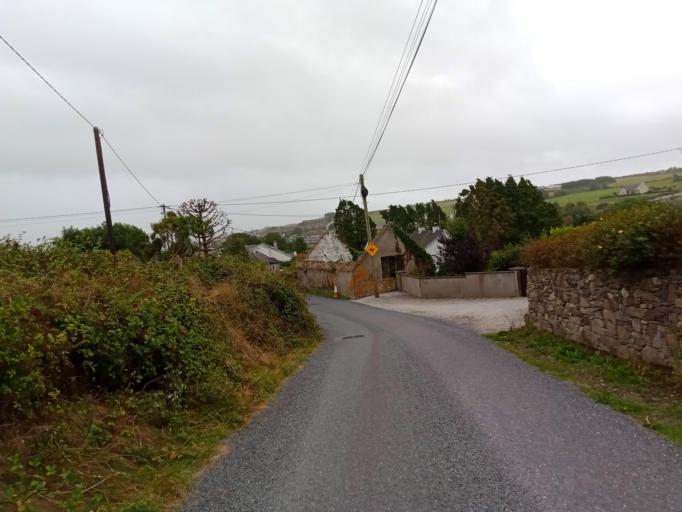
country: IE
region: Munster
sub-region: Waterford
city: Dungarvan
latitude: 52.0481
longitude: -7.5701
